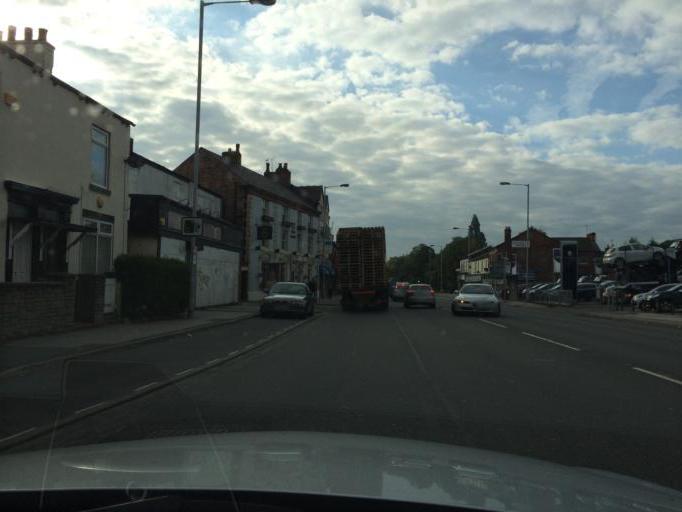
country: GB
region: England
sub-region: Borough of Stockport
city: Stockport
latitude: 53.3955
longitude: -2.1491
